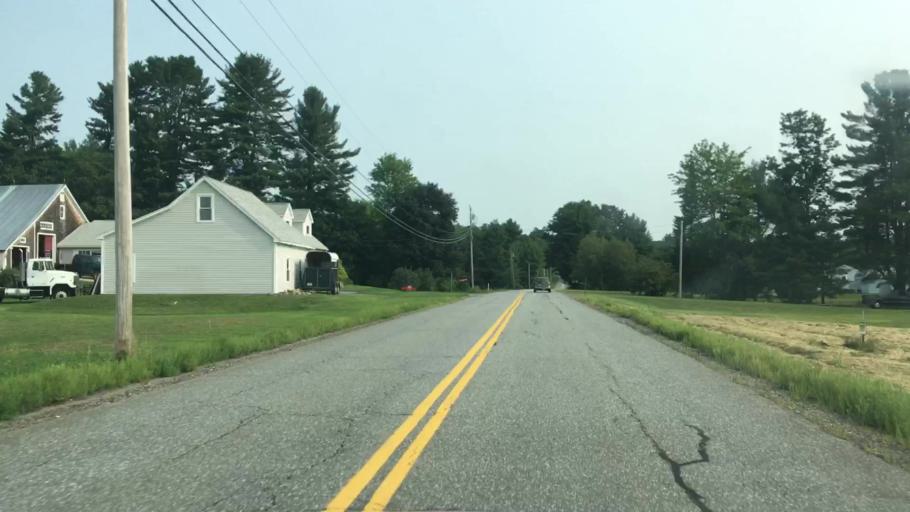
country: US
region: Maine
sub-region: Kennebec County
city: Chelsea
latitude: 44.3075
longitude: -69.6957
